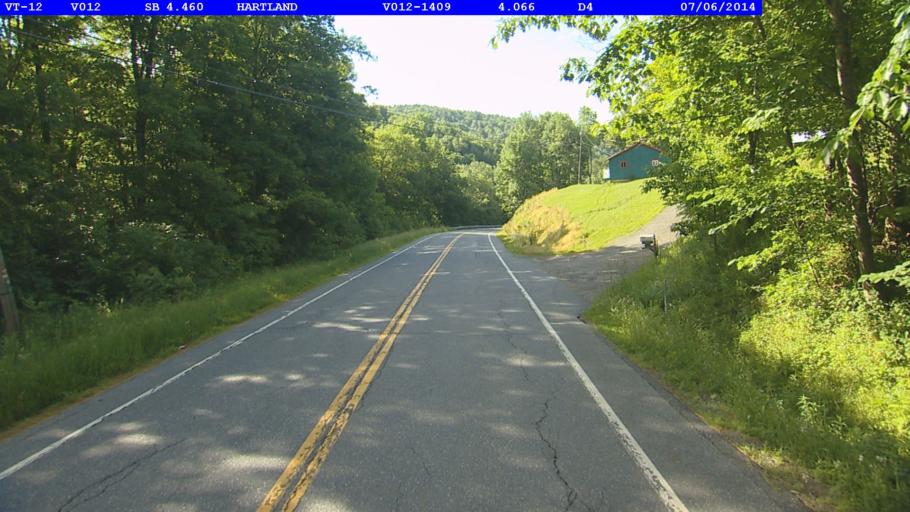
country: US
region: Vermont
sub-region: Windsor County
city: Woodstock
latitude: 43.5771
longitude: -72.4447
